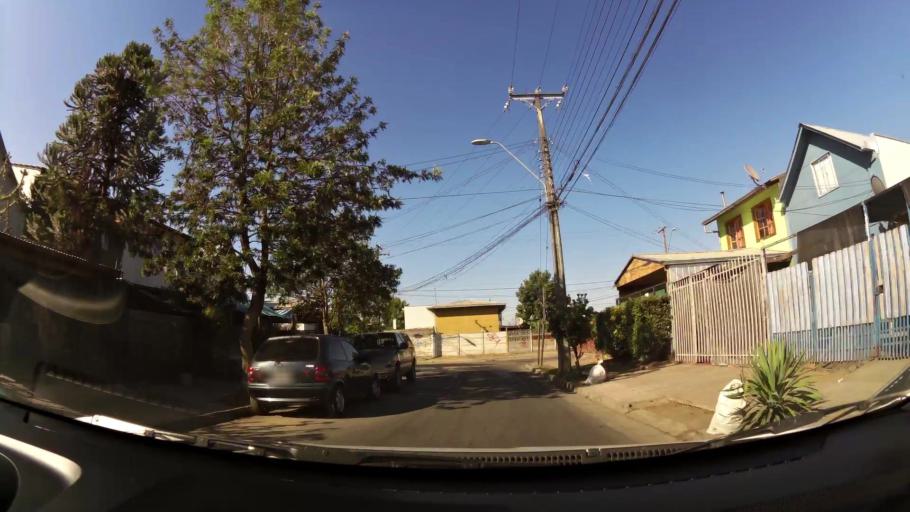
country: CL
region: Maule
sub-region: Provincia de Curico
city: Curico
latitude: -34.9925
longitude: -71.2599
